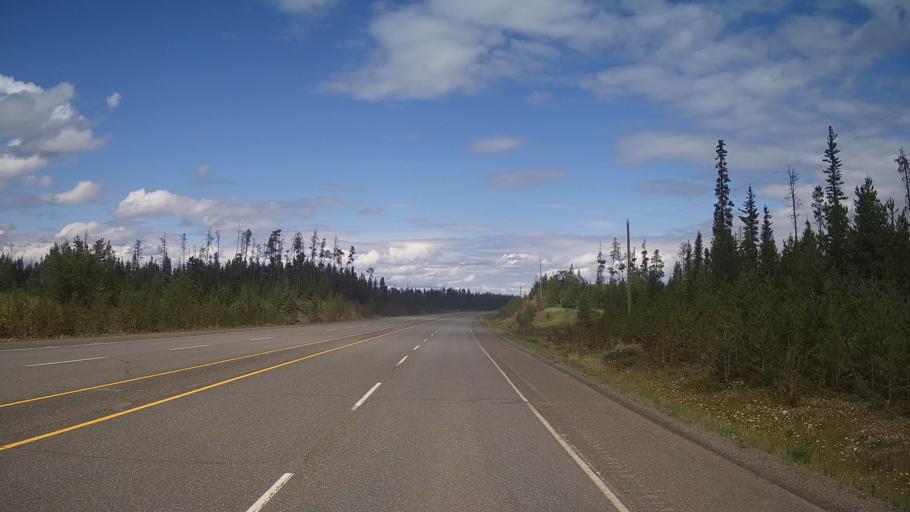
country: CA
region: British Columbia
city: Cache Creek
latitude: 51.5521
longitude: -121.3611
